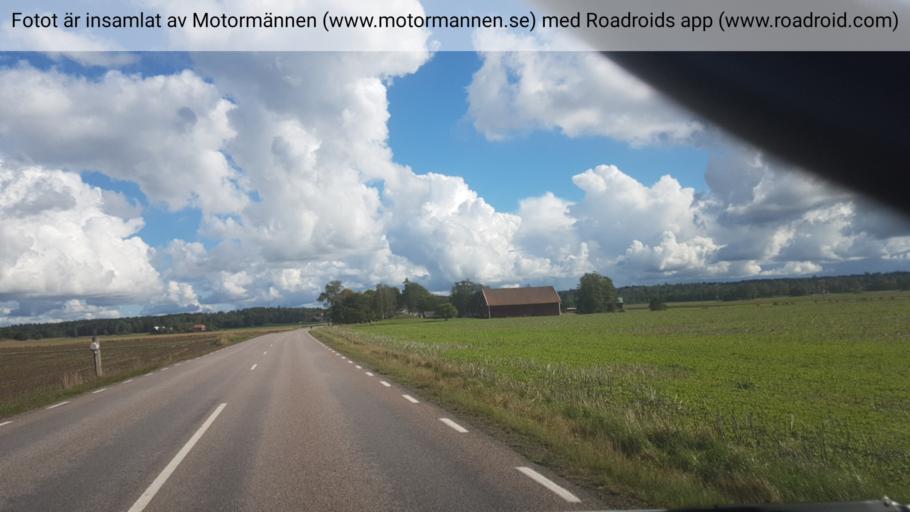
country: SE
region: Vaestra Goetaland
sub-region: Gotene Kommun
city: Goetene
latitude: 58.5434
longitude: 13.5820
